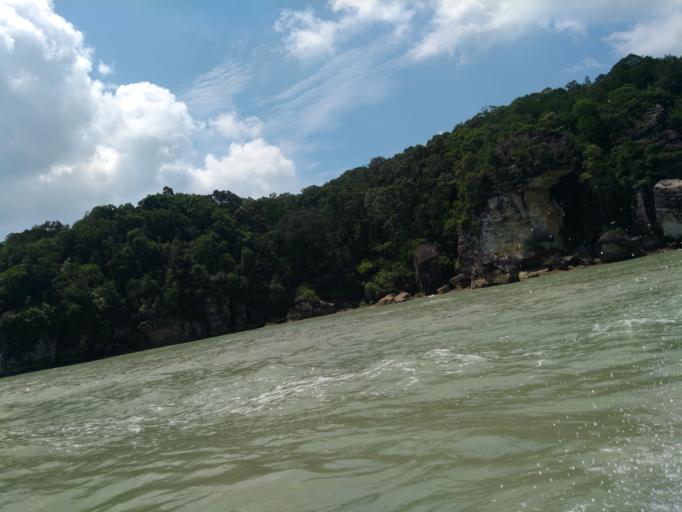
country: MY
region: Sarawak
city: Kuching
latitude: 1.7282
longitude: 110.4422
